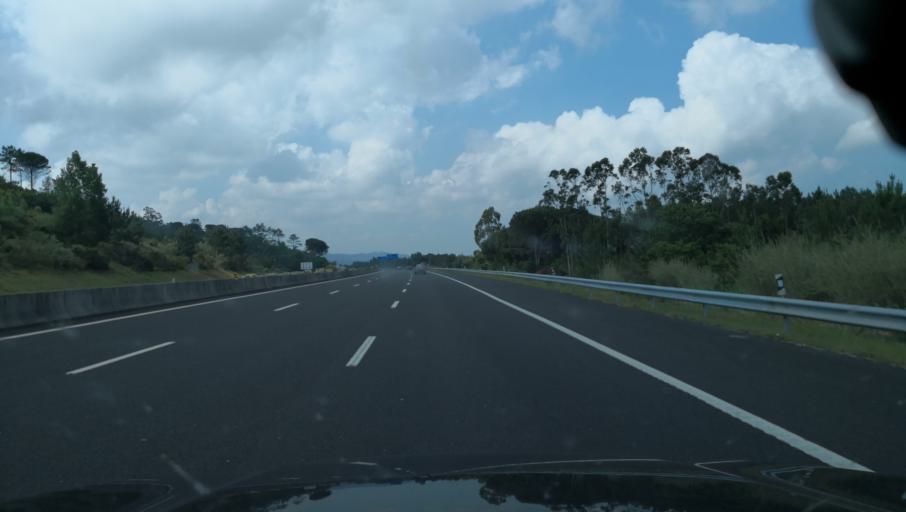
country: PT
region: Leiria
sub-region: Nazare
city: Nazare
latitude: 39.5194
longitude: -9.0857
